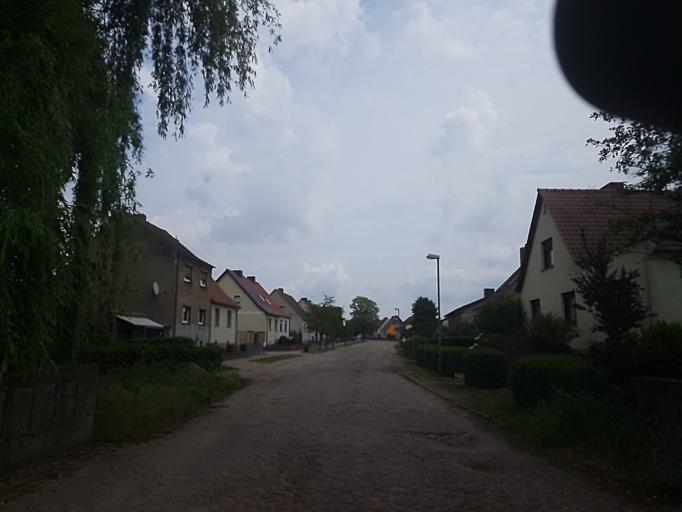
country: DE
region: Saxony-Anhalt
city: Loburg
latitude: 52.1174
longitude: 12.0916
